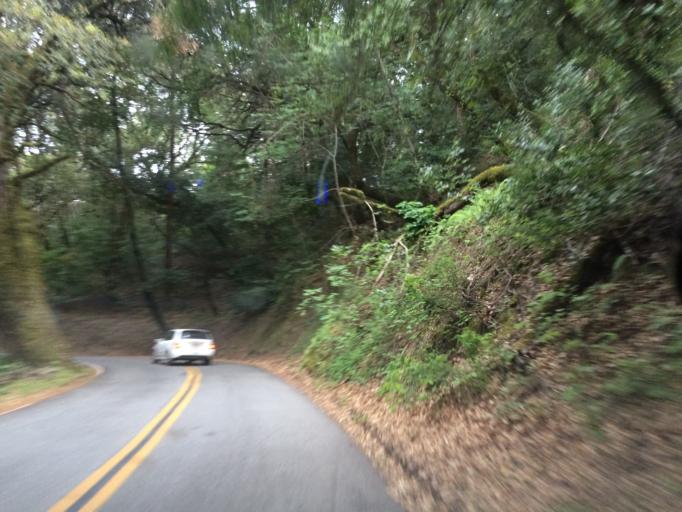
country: US
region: California
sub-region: Santa Clara County
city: Los Altos Hills
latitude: 37.3168
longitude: -122.1871
